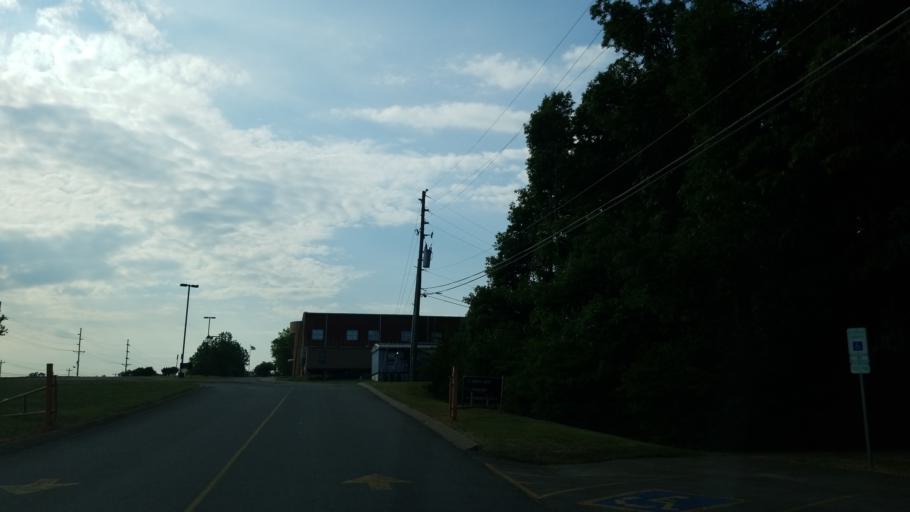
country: US
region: Tennessee
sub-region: Rutherford County
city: La Vergne
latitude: 36.0400
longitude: -86.6026
